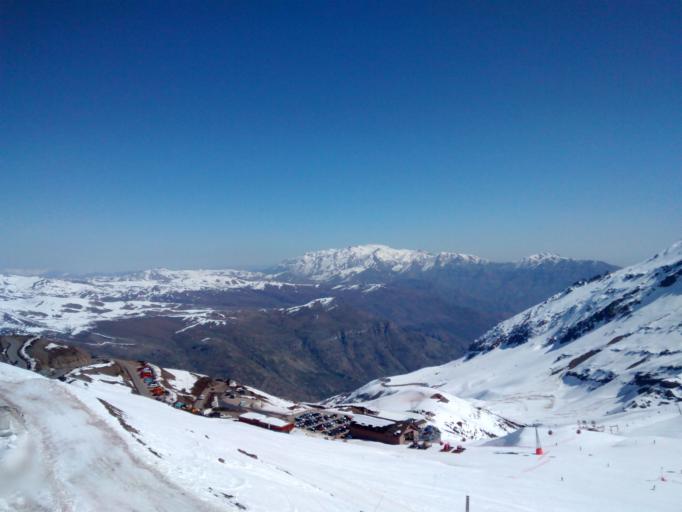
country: CL
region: Santiago Metropolitan
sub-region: Provincia de Santiago
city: Villa Presidente Frei, Nunoa, Santiago, Chile
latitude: -33.3538
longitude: -70.2492
